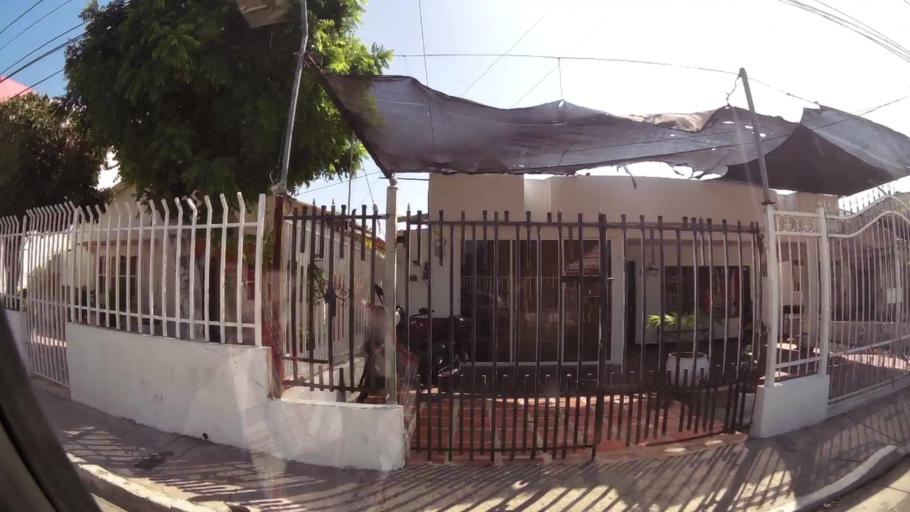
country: CO
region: Bolivar
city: Cartagena
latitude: 10.4395
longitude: -75.5202
